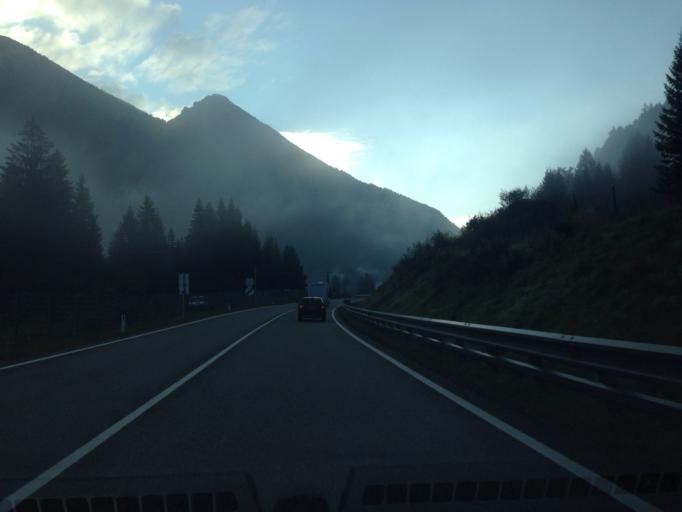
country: AT
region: Tyrol
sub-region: Politischer Bezirk Reutte
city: Heiterwang
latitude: 47.4377
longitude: 10.7559
